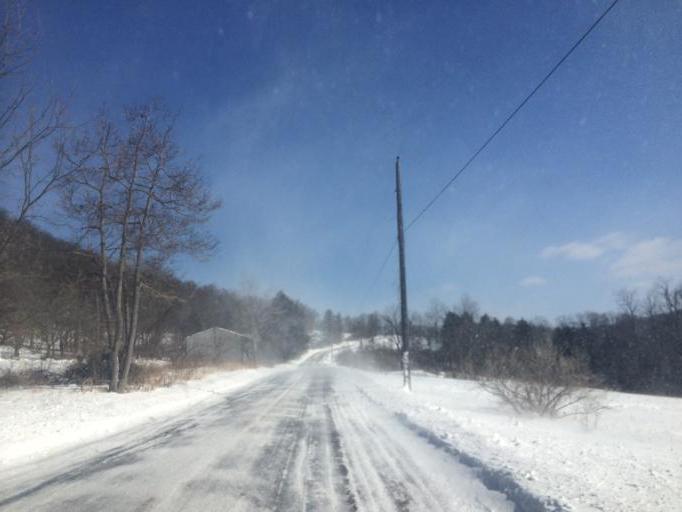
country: US
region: Pennsylvania
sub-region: Centre County
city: Stormstown
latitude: 40.8701
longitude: -78.0272
